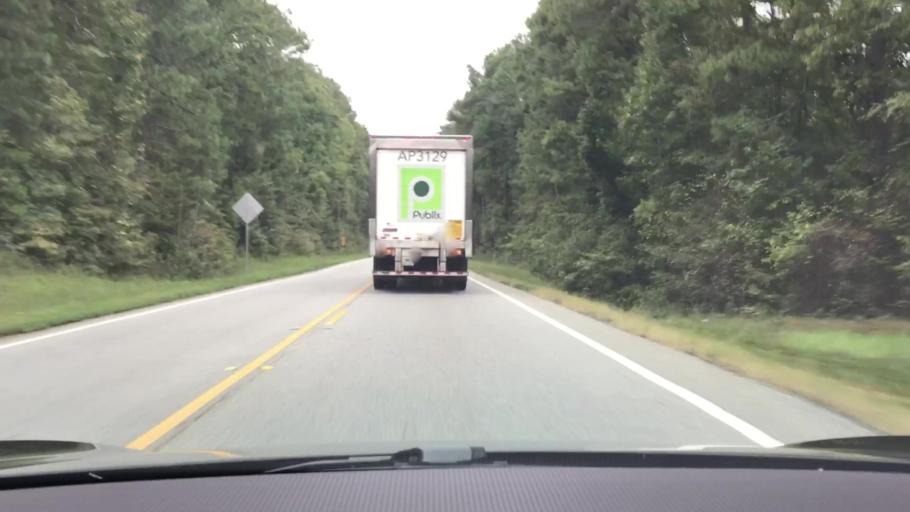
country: US
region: Georgia
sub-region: Greene County
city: Greensboro
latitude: 33.6972
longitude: -83.2791
